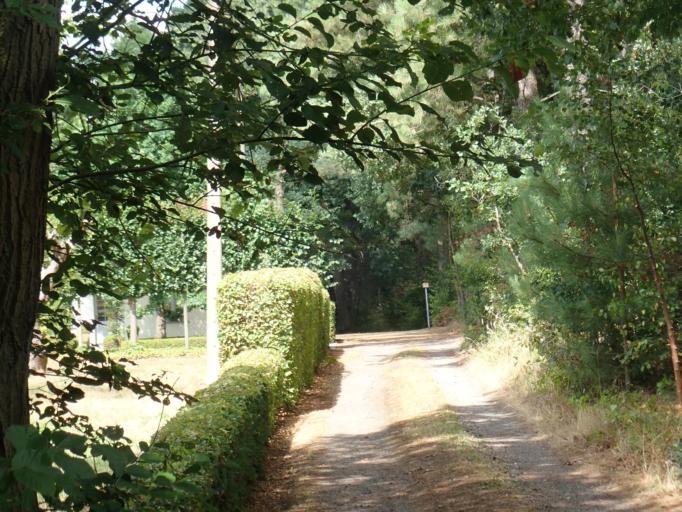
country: BE
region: Flanders
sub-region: Provincie Antwerpen
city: Herselt
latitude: 51.0566
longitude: 4.9097
